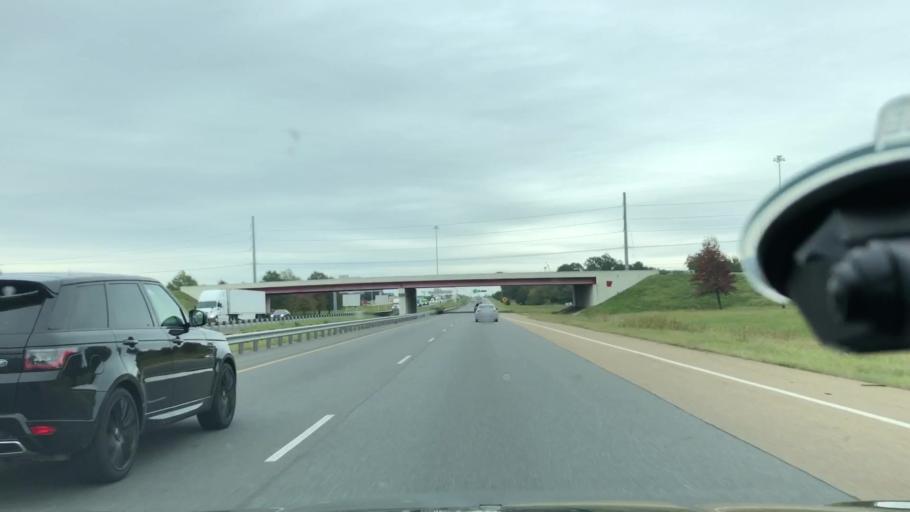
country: US
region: Arkansas
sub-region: Miller County
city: Texarkana
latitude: 33.4709
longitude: -94.0307
